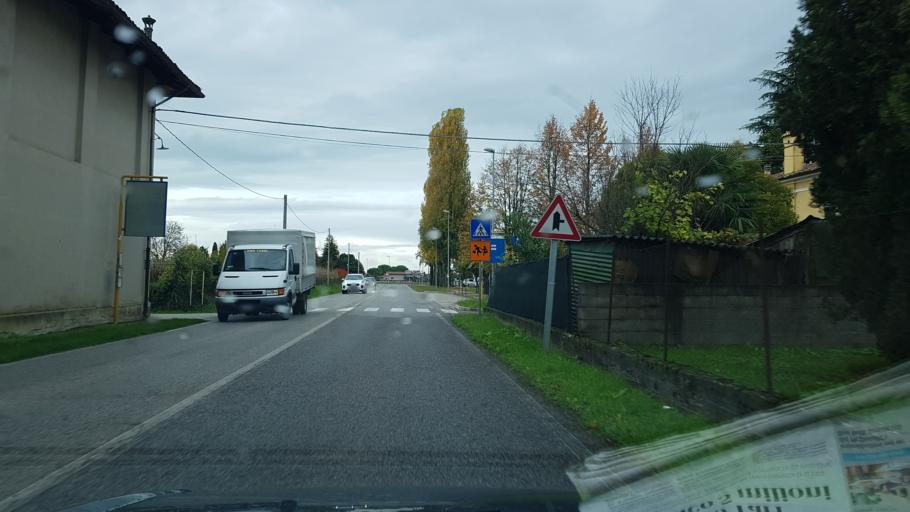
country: IT
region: Friuli Venezia Giulia
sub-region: Provincia di Udine
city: Fiumicello
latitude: 45.8005
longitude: 13.4042
